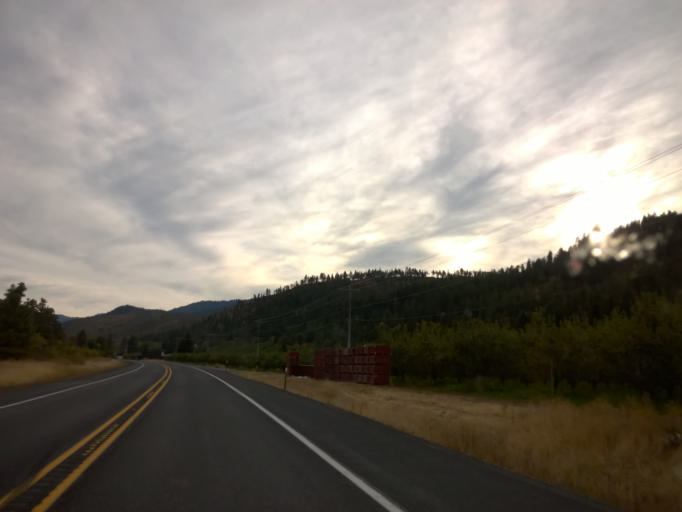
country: US
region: Washington
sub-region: Chelan County
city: Leavenworth
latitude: 47.5444
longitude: -120.6163
